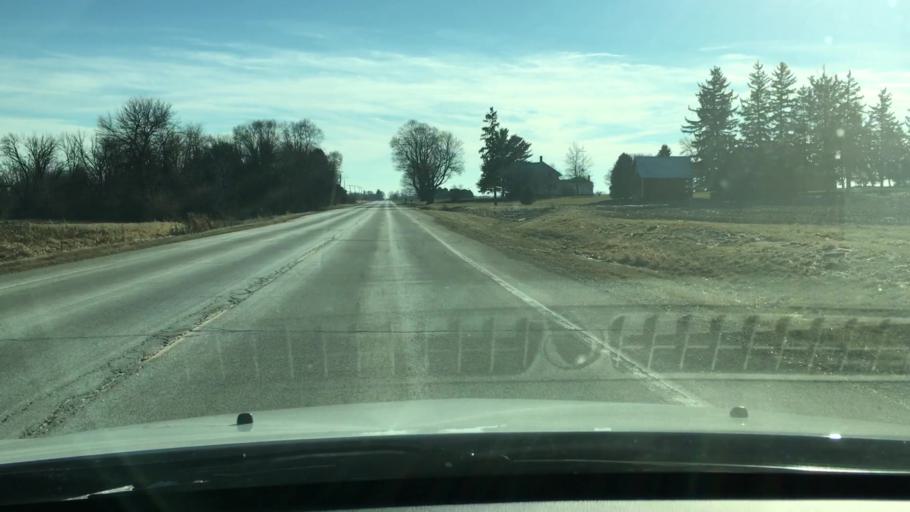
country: US
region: Illinois
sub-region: LaSalle County
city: Mendota
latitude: 41.5838
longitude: -89.1283
